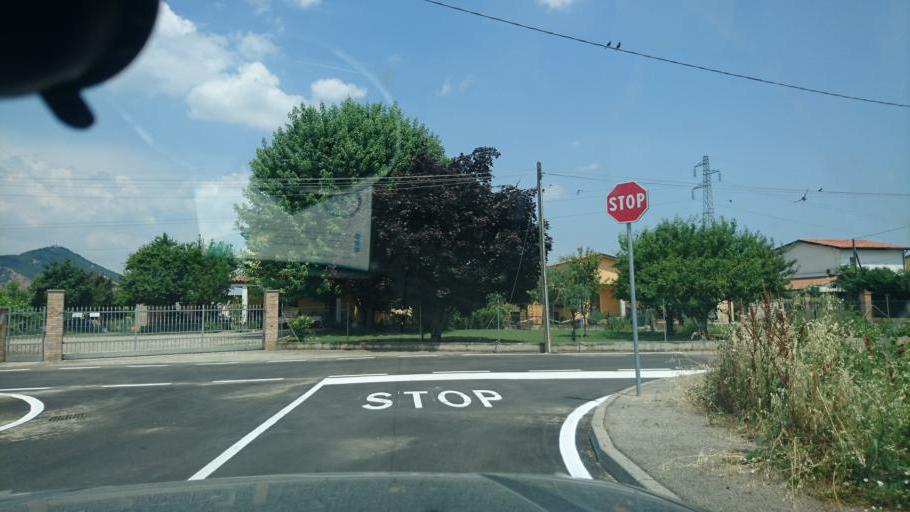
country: IT
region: Veneto
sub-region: Provincia di Padova
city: Monselice
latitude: 45.2239
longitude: 11.7402
